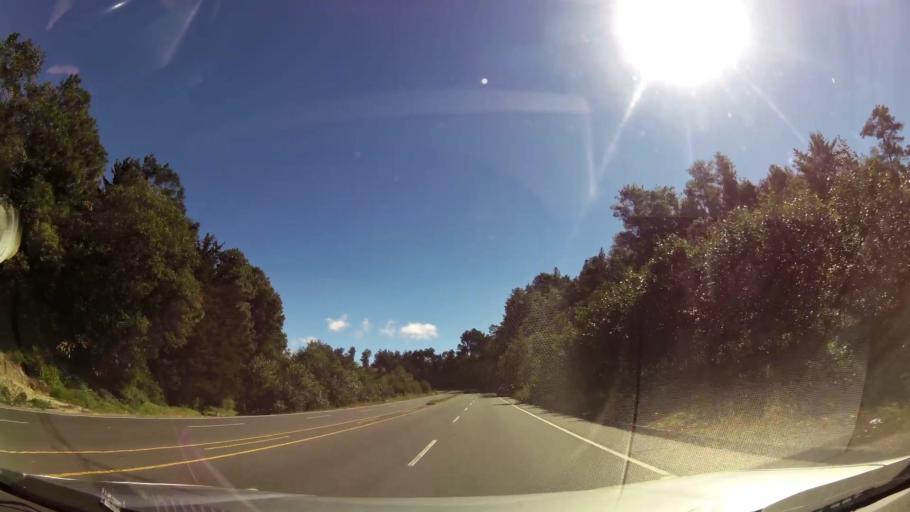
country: GT
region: Solola
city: Solola
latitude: 14.8149
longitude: -91.2051
